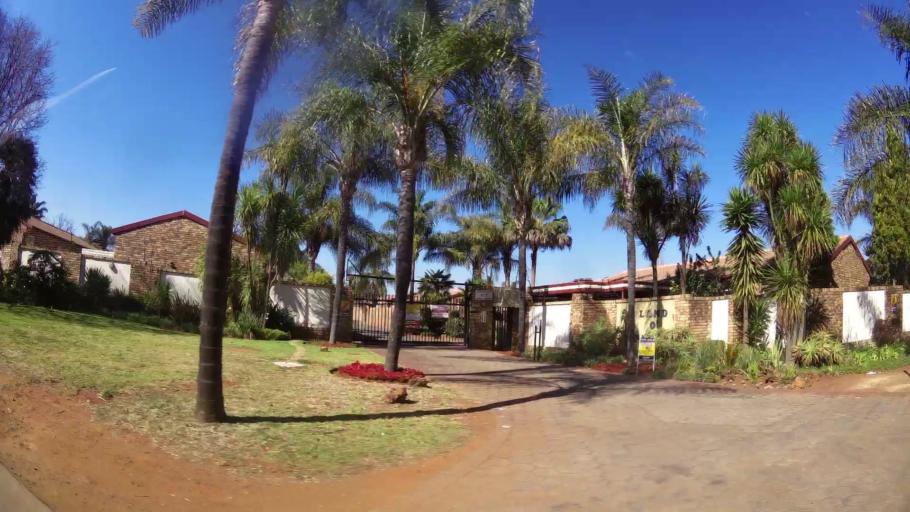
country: ZA
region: Gauteng
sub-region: City of Tshwane Metropolitan Municipality
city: Centurion
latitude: -25.8543
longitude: 28.2017
